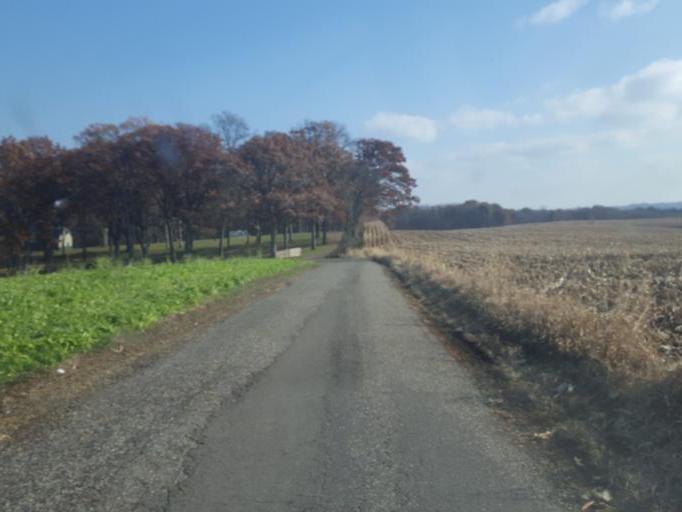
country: US
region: Ohio
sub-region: Ashland County
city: Loudonville
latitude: 40.6166
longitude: -82.2169
